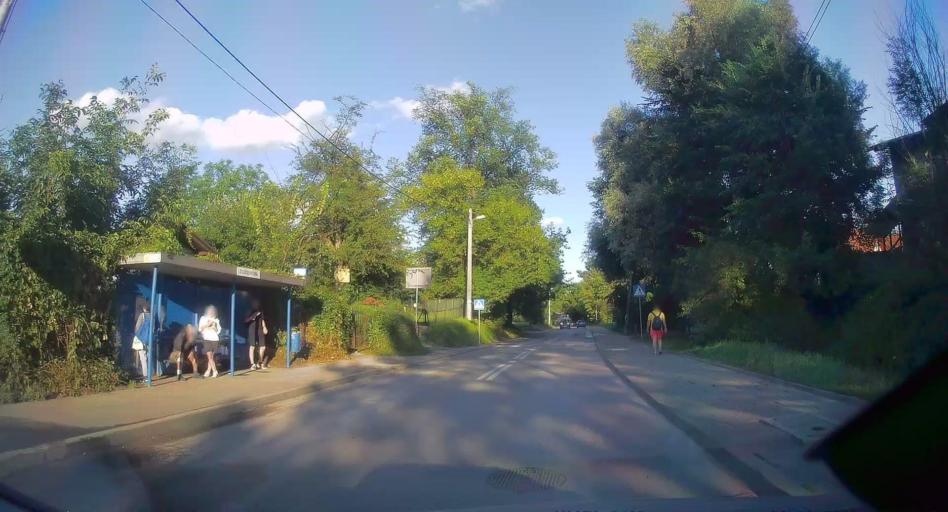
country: PL
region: Lesser Poland Voivodeship
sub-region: Powiat wielicki
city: Czarnochowice
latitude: 50.0163
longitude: 20.0505
